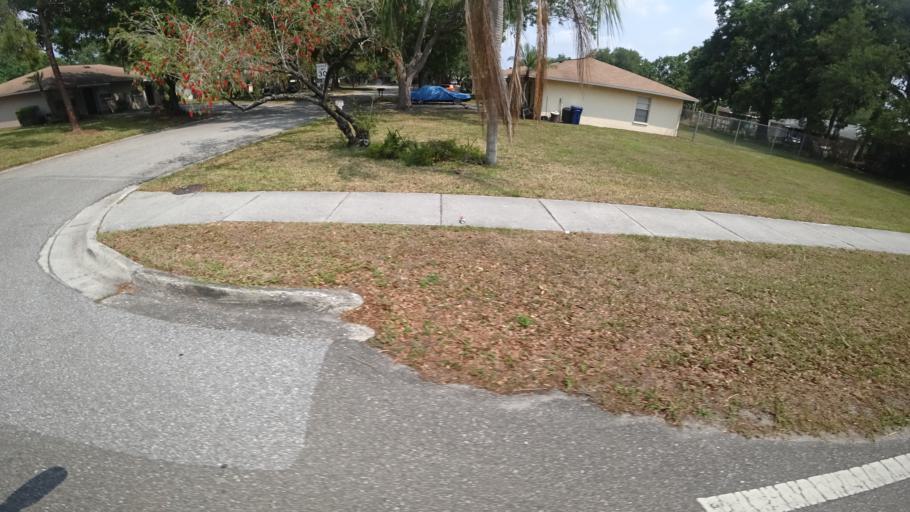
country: US
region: Florida
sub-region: Manatee County
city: Samoset
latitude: 27.4770
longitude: -82.5430
